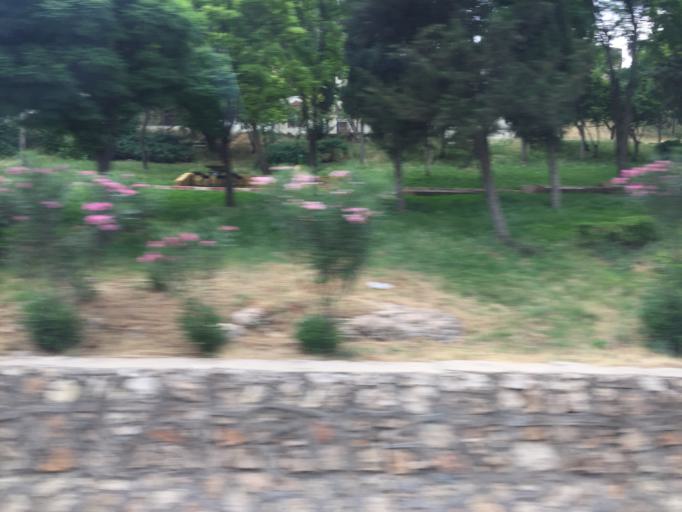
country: TR
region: Gaziantep
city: Gaziantep
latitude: 37.0535
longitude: 37.4194
